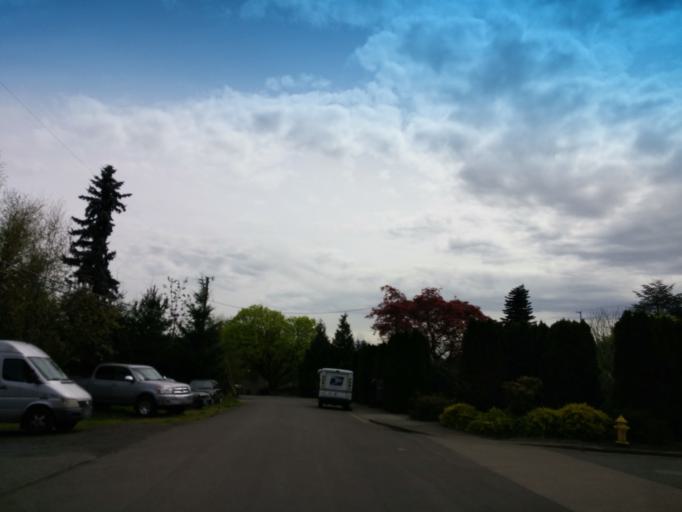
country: US
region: Oregon
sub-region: Washington County
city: Cedar Mill
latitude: 45.5224
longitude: -122.8123
